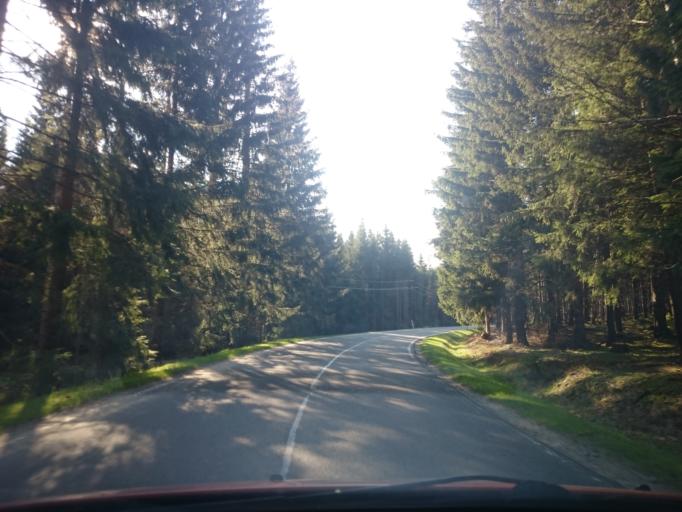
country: PL
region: Lower Silesian Voivodeship
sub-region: Powiat klodzki
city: Szczytna
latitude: 50.3222
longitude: 16.4361
